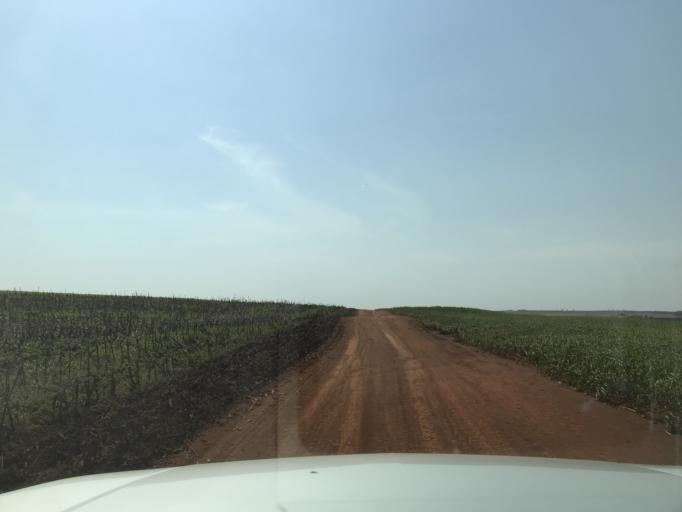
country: BR
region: Parana
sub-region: Palotina
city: Palotina
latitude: -24.2301
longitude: -53.7424
